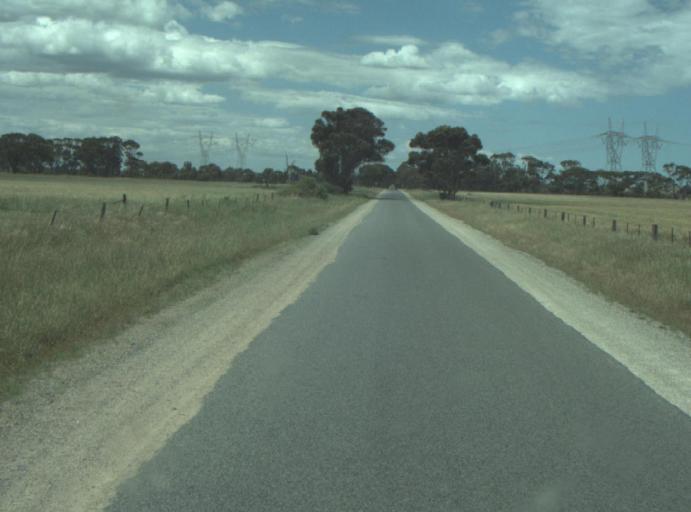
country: AU
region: Victoria
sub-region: Wyndham
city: Little River
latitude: -37.8758
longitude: 144.3996
